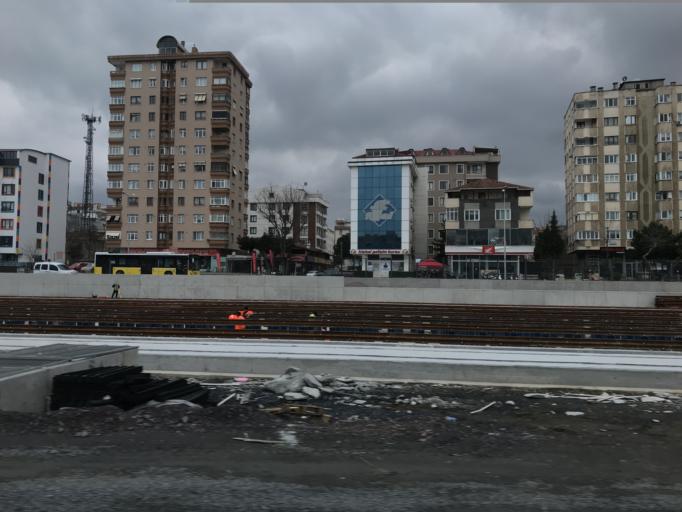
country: TR
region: Istanbul
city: Pendik
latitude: 40.8808
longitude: 29.2300
